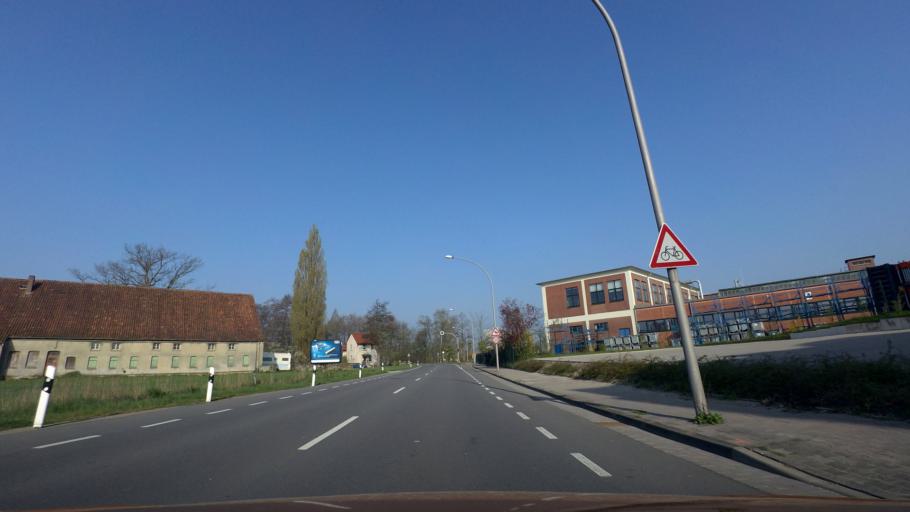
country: DE
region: Lower Saxony
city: Melle
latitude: 52.2094
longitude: 8.3288
